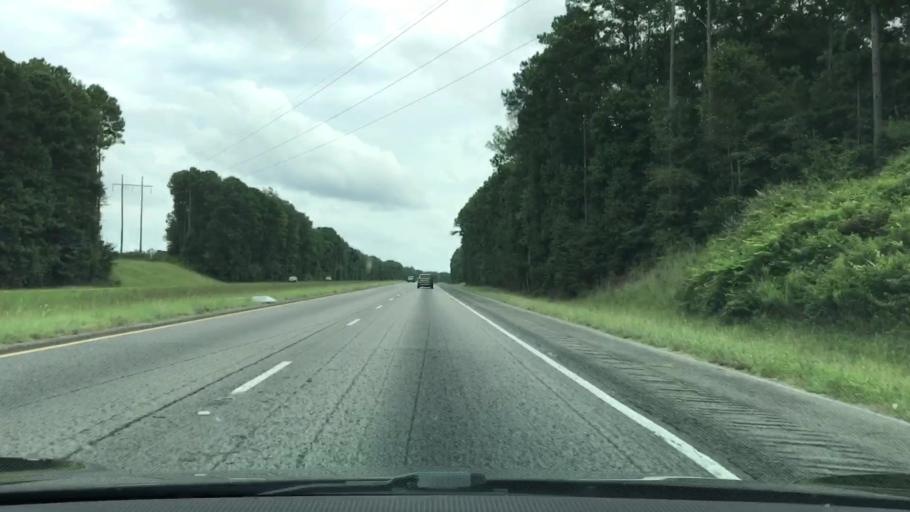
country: US
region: Georgia
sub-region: Troup County
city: La Grange
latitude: 32.9750
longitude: -85.0605
